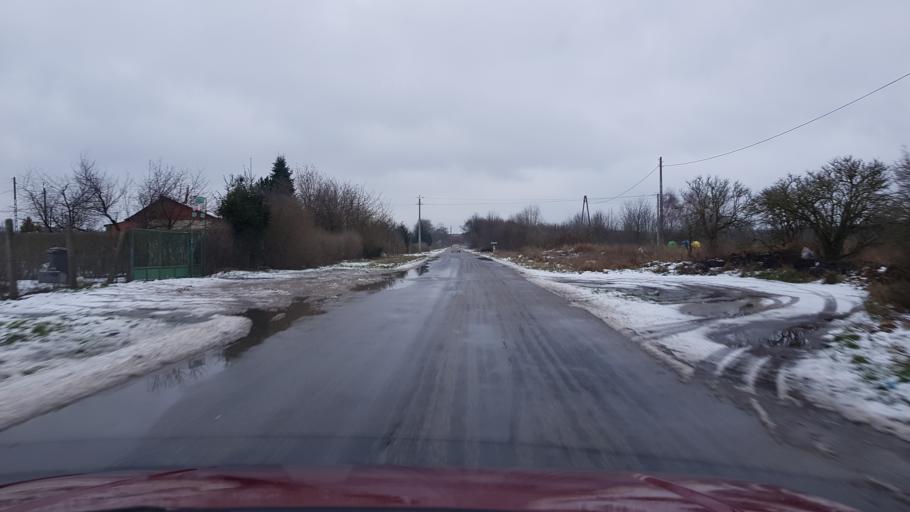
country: PL
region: West Pomeranian Voivodeship
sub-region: Powiat goleniowski
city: Nowogard
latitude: 53.6572
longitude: 15.1244
